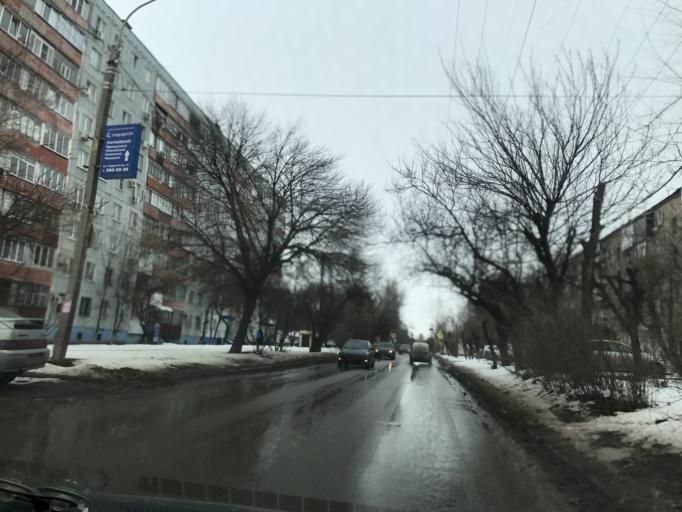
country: RU
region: Rostov
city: Rostov-na-Donu
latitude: 47.2280
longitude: 39.6334
